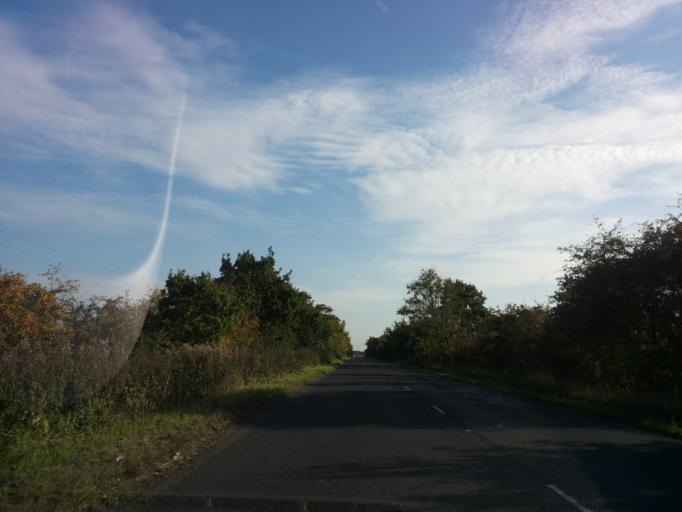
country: GB
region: England
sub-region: Doncaster
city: Hatfield
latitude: 53.5985
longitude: -0.9662
